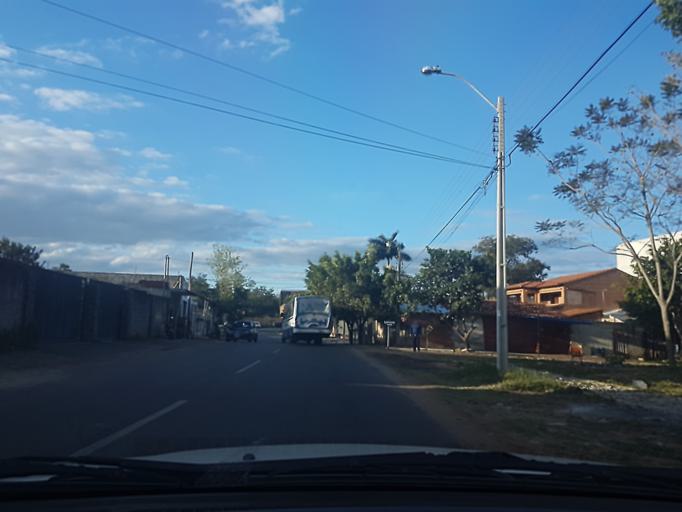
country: PY
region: Central
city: Colonia Mariano Roque Alonso
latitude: -25.2363
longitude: -57.5381
